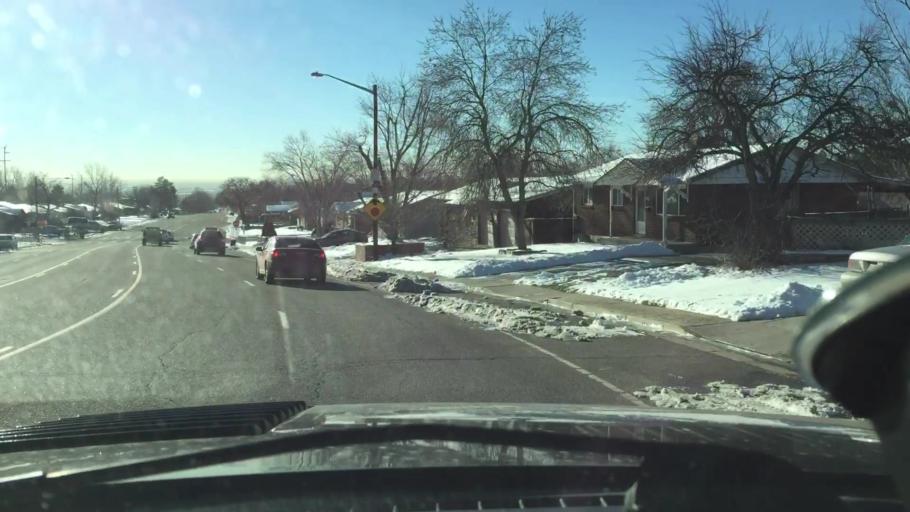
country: US
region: Colorado
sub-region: Adams County
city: Sherrelwood
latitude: 39.8404
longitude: -105.0018
